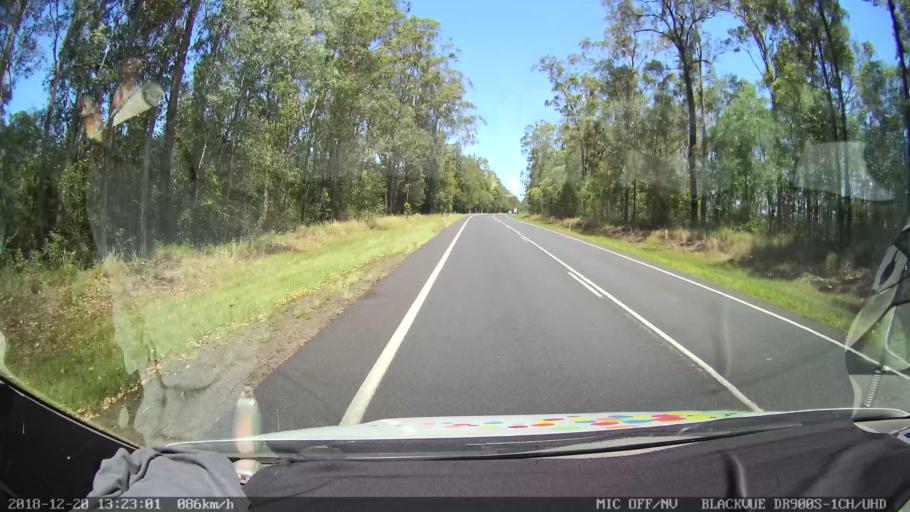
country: AU
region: New South Wales
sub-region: Richmond Valley
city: Casino
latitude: -29.0990
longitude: 153.0009
